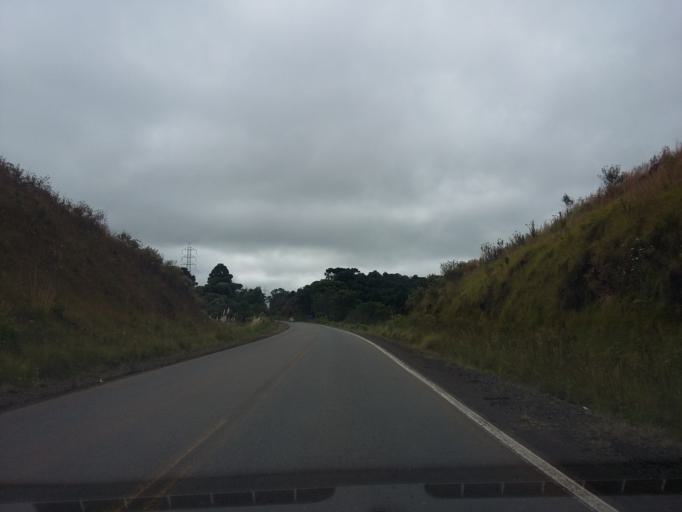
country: BR
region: Santa Catarina
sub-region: Lages
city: Lages
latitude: -27.8886
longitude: -50.1591
